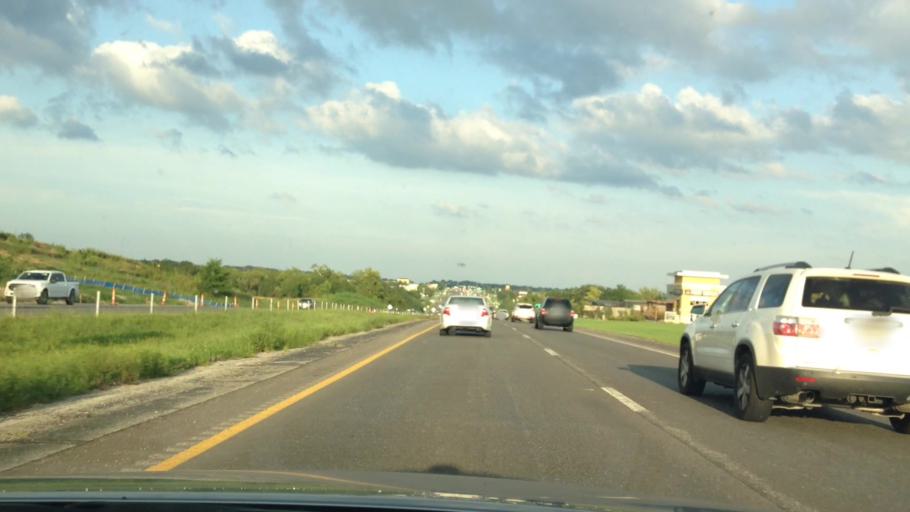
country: US
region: Missouri
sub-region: Clay County
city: Pleasant Valley
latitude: 39.2449
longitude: -94.4760
